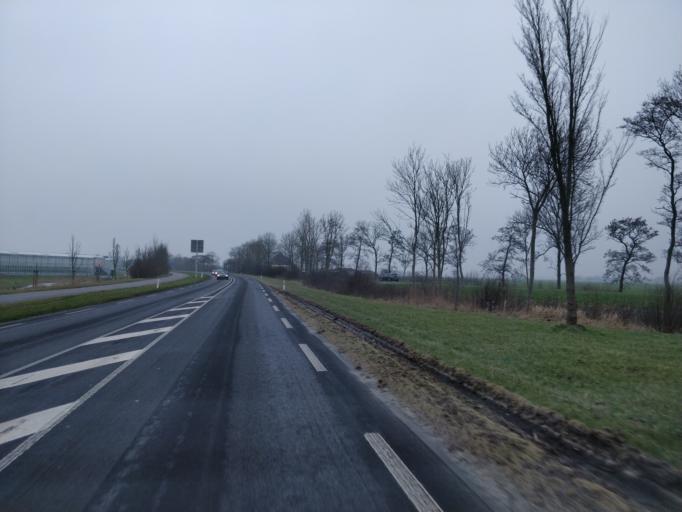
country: NL
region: Friesland
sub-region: Menameradiel
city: Menaam
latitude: 53.2387
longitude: 5.6770
